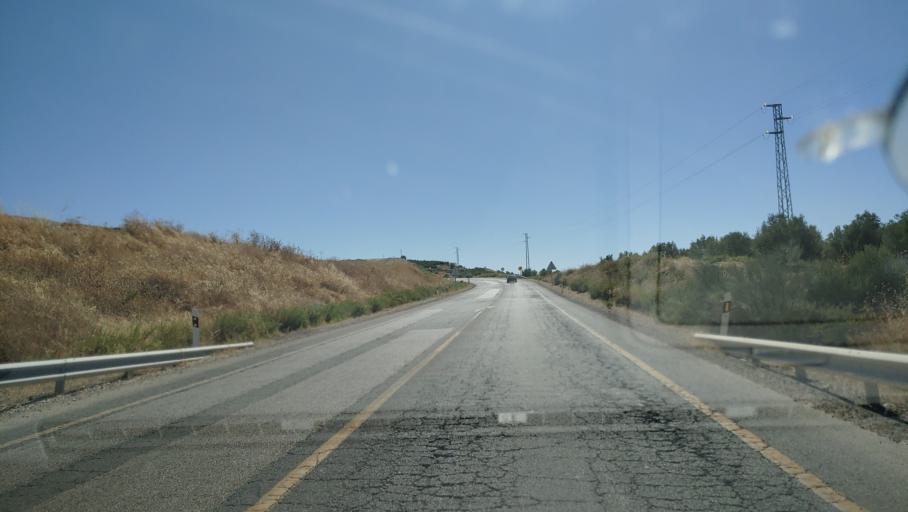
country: ES
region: Andalusia
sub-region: Provincia de Jaen
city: Iznatoraf
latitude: 38.1380
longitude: -3.0480
